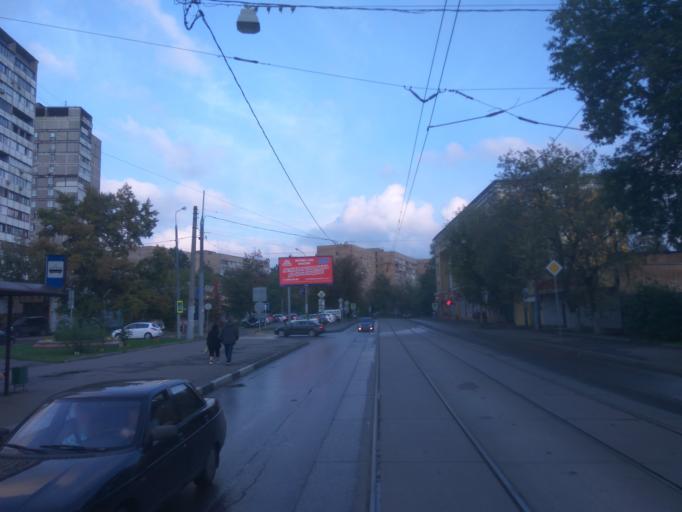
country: RU
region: Moskovskaya
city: Bogorodskoye
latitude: 55.8100
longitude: 37.7038
